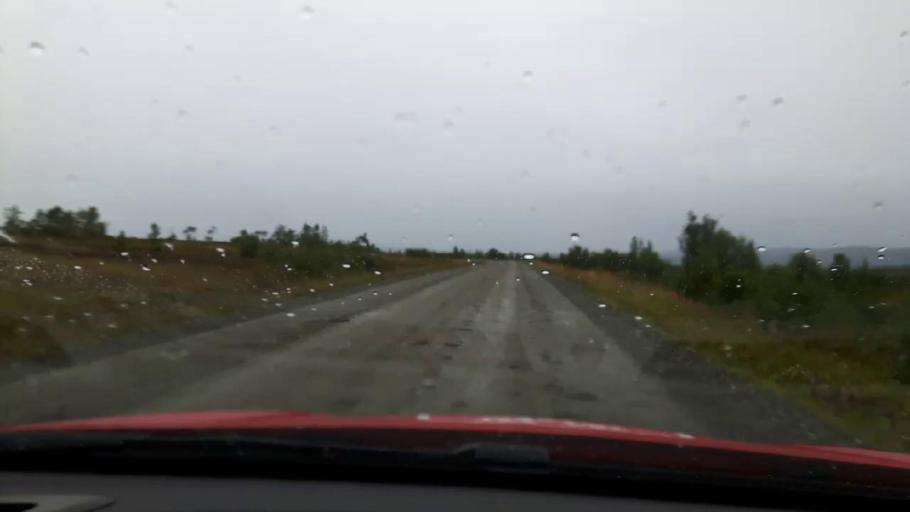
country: NO
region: Nord-Trondelag
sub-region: Meraker
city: Meraker
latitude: 63.6084
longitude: 12.2756
